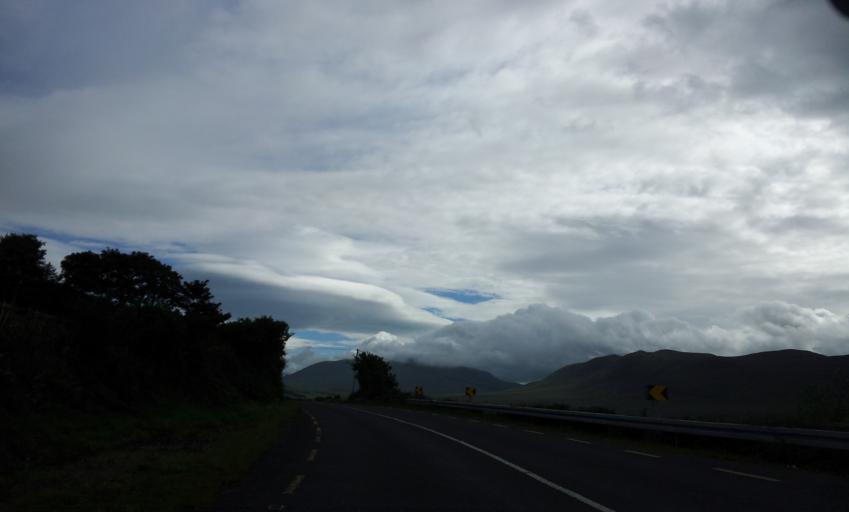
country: IE
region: Munster
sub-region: Ciarrai
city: Killorglin
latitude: 52.1732
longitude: -9.9949
